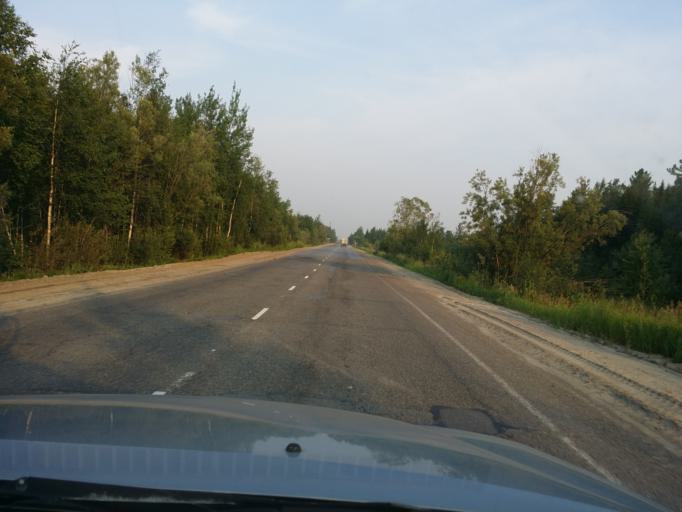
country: RU
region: Khanty-Mansiyskiy Avtonomnyy Okrug
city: Nizhnevartovsk
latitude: 61.2004
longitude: 76.5398
